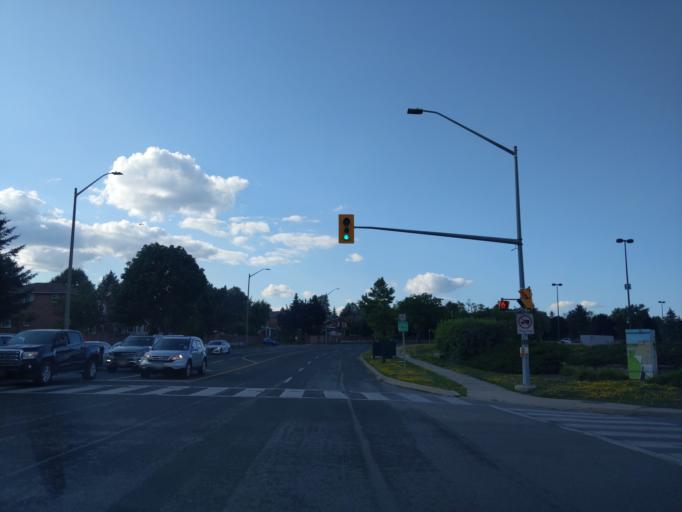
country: CA
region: Ontario
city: Markham
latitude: 43.8674
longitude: -79.2927
